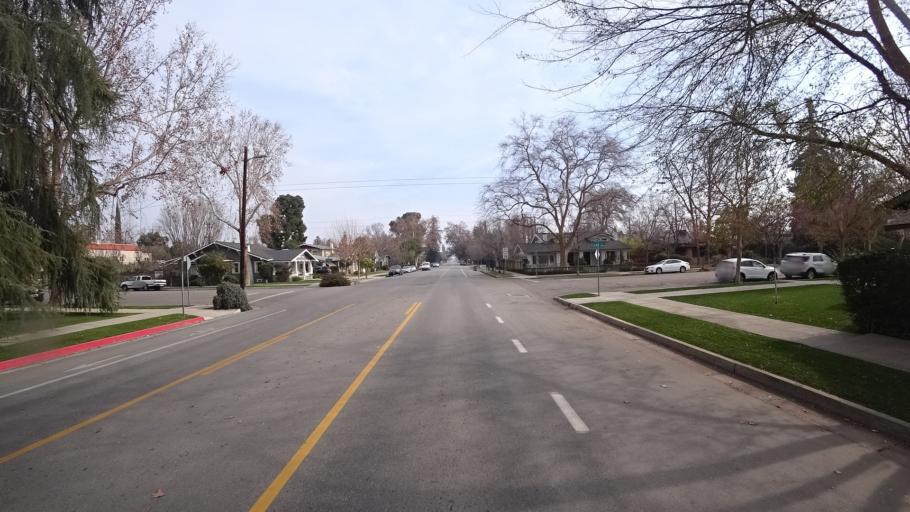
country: US
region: California
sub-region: Kern County
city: Bakersfield
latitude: 35.3782
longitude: -119.0308
